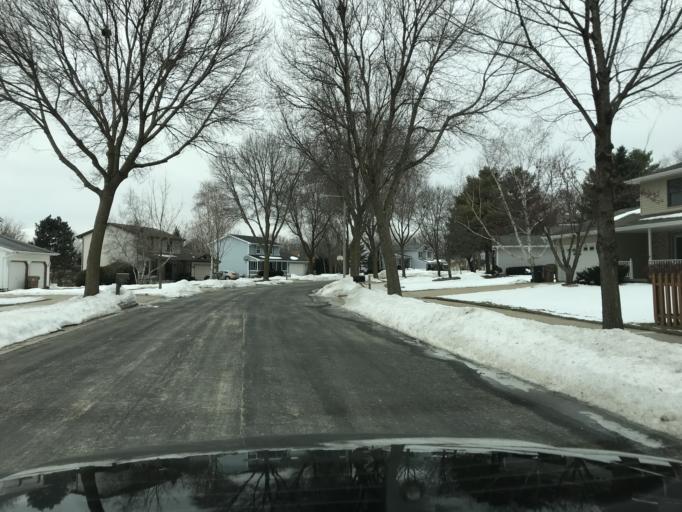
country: US
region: Wisconsin
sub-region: Dane County
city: Monona
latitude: 43.0691
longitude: -89.2842
